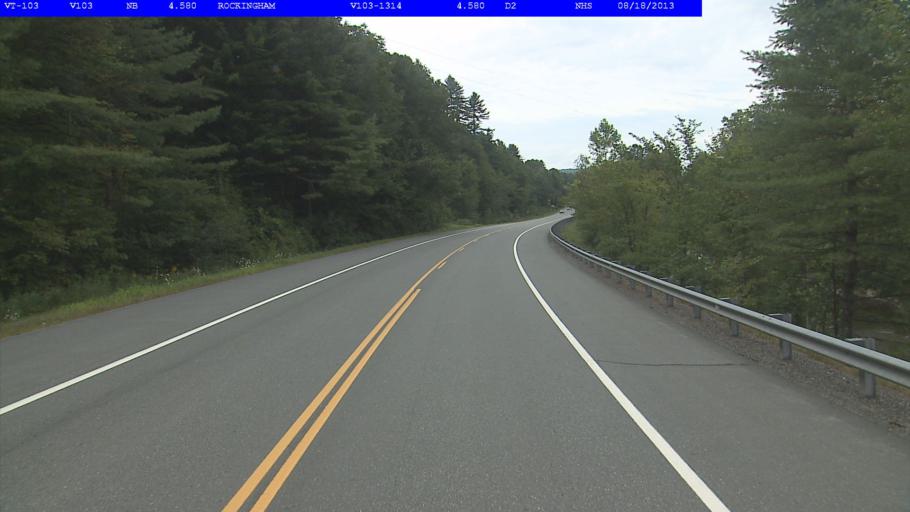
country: US
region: Vermont
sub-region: Windham County
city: Rockingham
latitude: 43.2077
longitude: -72.5372
